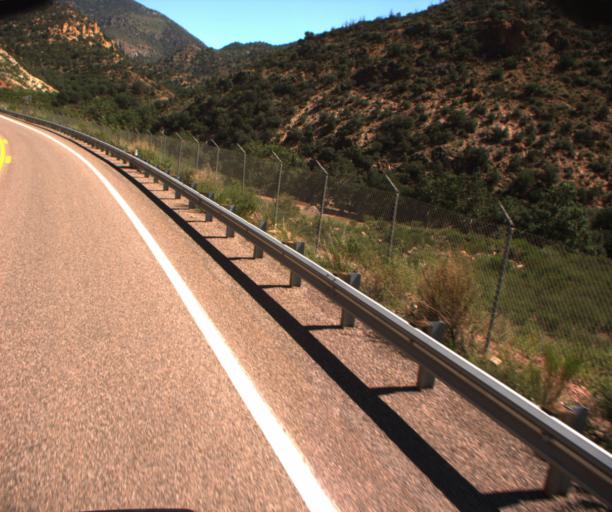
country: US
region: Arizona
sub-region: Greenlee County
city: Morenci
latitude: 33.1500
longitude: -109.3750
